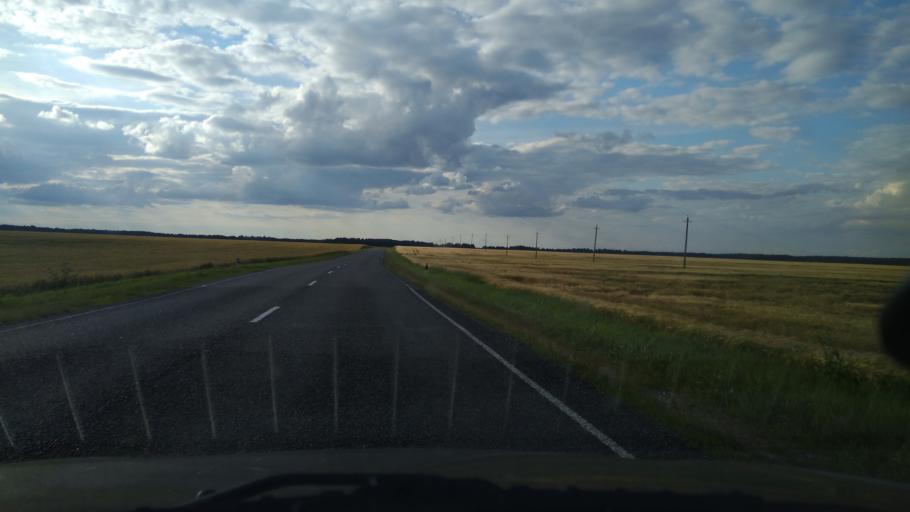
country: BY
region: Grodnenskaya
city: Masty
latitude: 53.3281
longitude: 24.6788
